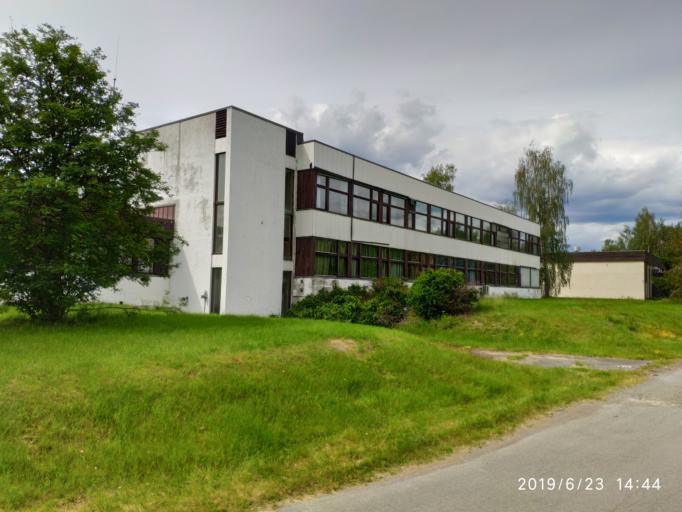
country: NO
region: Buskerud
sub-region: Ringerike
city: Honefoss
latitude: 60.1911
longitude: 10.2985
